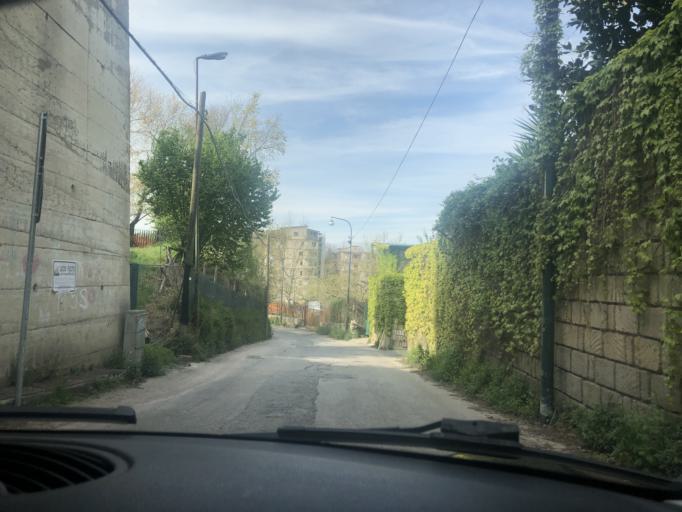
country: IT
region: Campania
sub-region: Provincia di Napoli
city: Torre Caracciolo
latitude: 40.8699
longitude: 14.1932
